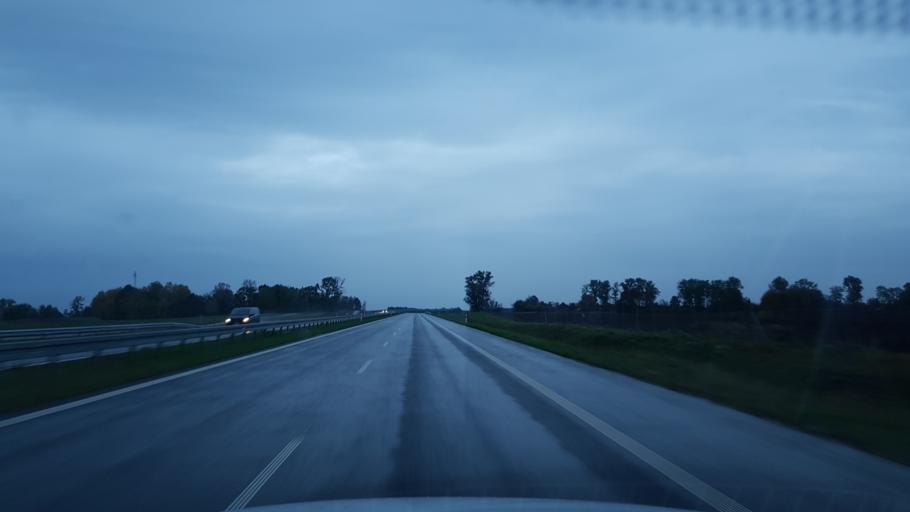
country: PL
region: West Pomeranian Voivodeship
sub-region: Powiat kolobrzeski
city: Ryman
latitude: 54.0172
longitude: 15.4773
